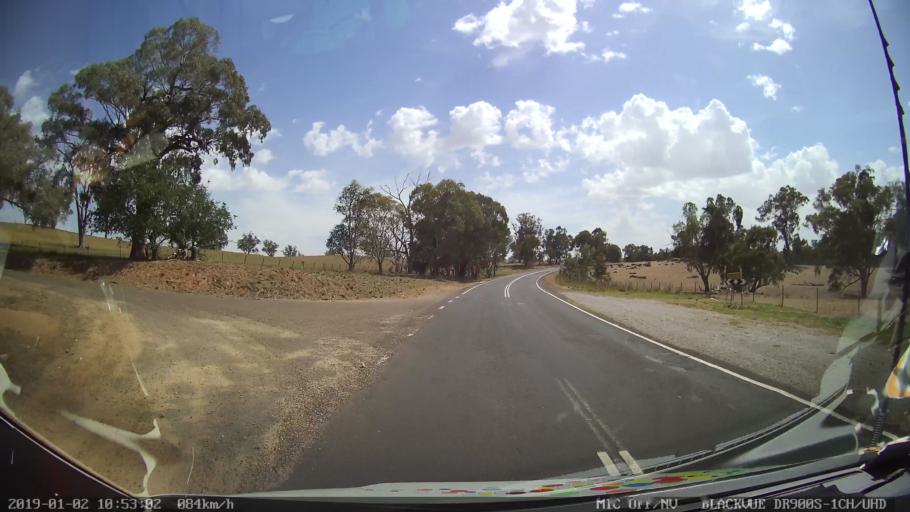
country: AU
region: New South Wales
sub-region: Cootamundra
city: Cootamundra
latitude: -34.6819
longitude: 148.2717
